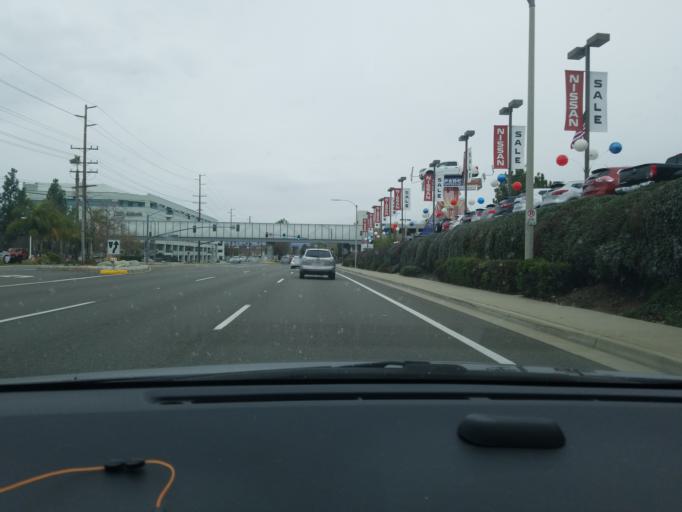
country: US
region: California
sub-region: Riverside County
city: Temecula
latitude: 33.5161
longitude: -117.1555
